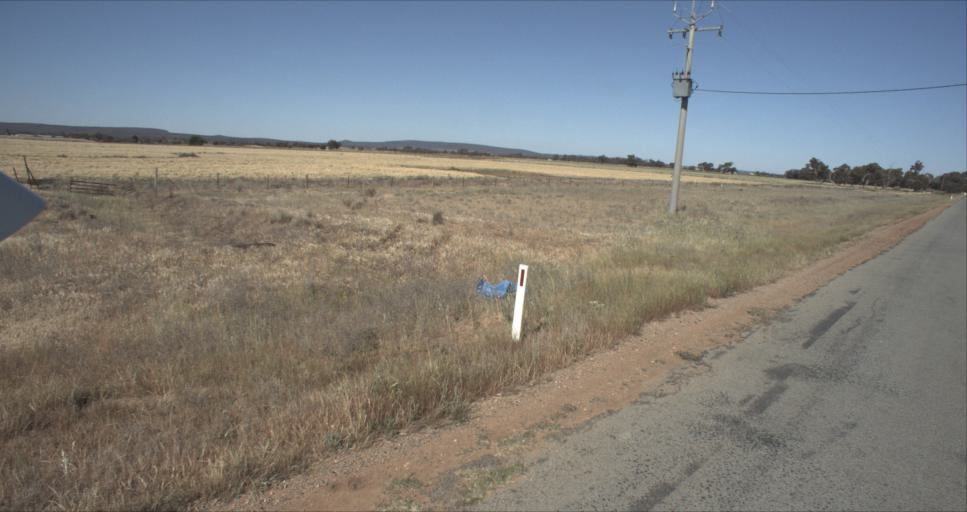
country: AU
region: New South Wales
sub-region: Leeton
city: Leeton
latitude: -34.4970
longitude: 146.3905
